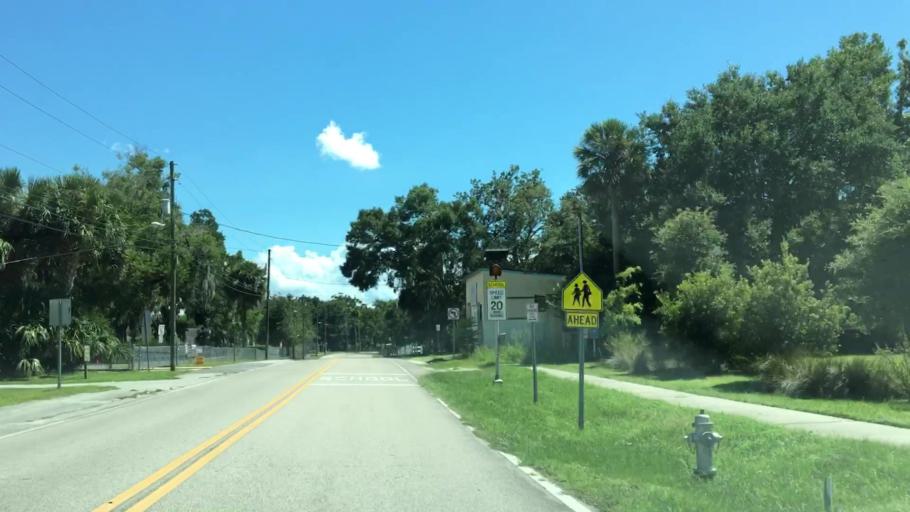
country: US
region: Florida
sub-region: Volusia County
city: Deltona
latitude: 28.8729
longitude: -81.2662
